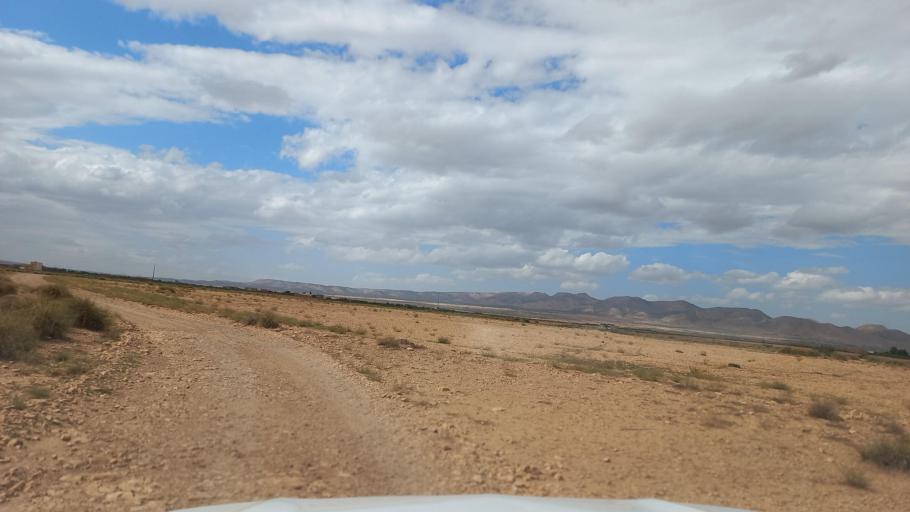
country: TN
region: Al Qasrayn
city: Sbiba
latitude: 35.3808
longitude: 9.1027
